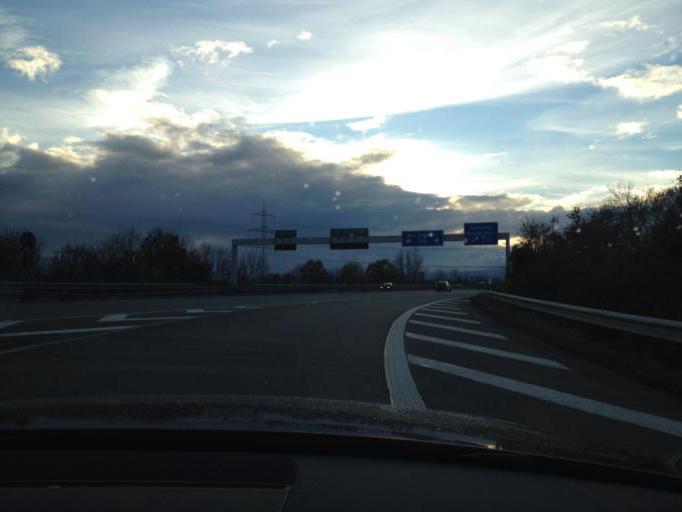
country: DE
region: Rheinland-Pfalz
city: Maxdorf
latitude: 49.4779
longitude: 8.3142
